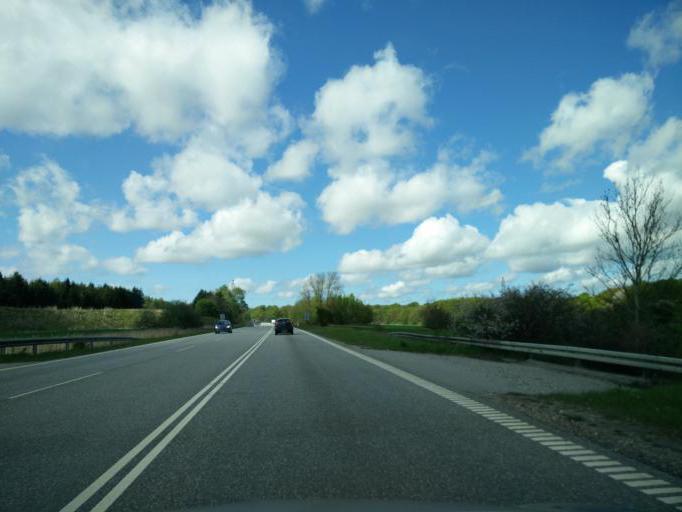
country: DK
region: Capital Region
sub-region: Allerod Kommune
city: Lillerod
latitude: 55.8783
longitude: 12.3064
